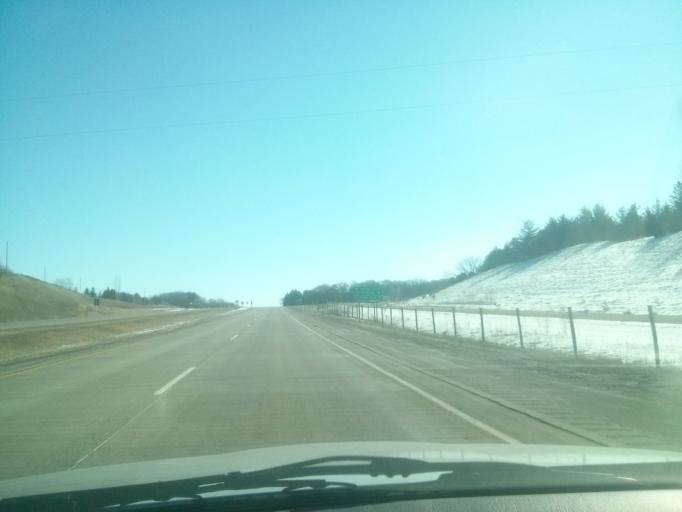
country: US
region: Wisconsin
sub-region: Saint Croix County
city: Somerset
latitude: 45.1229
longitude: -92.6336
